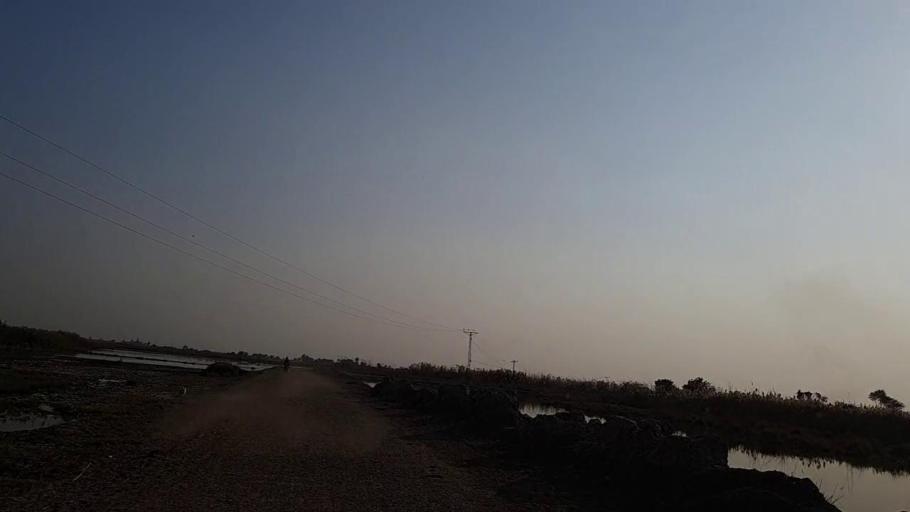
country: PK
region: Sindh
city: Sakrand
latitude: 26.0918
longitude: 68.3935
